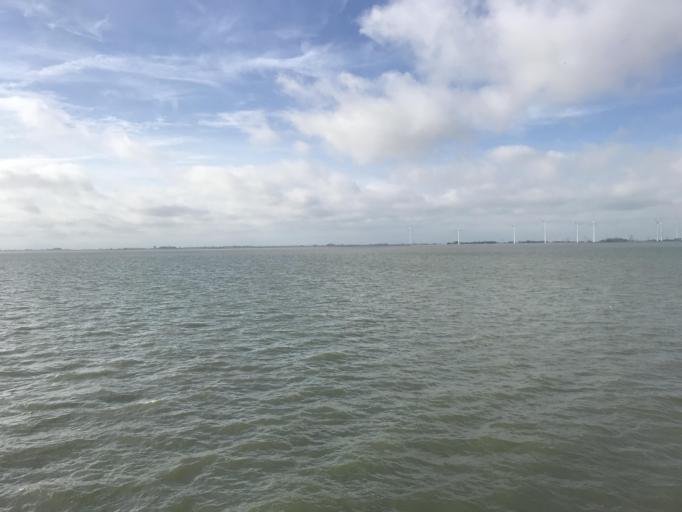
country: NL
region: Groningen
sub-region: Gemeente Delfzijl
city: Delfzijl
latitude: 53.4251
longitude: 6.9243
